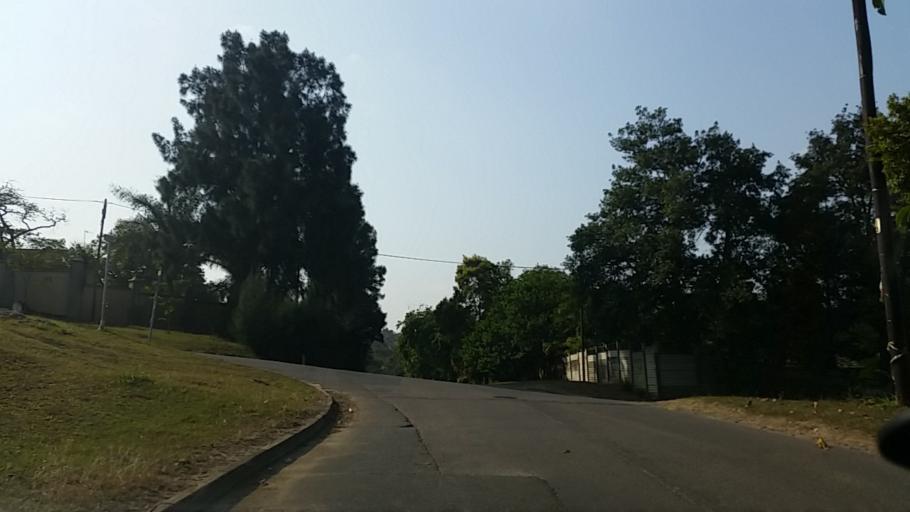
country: ZA
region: KwaZulu-Natal
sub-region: eThekwini Metropolitan Municipality
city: Berea
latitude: -29.8397
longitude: 30.9501
